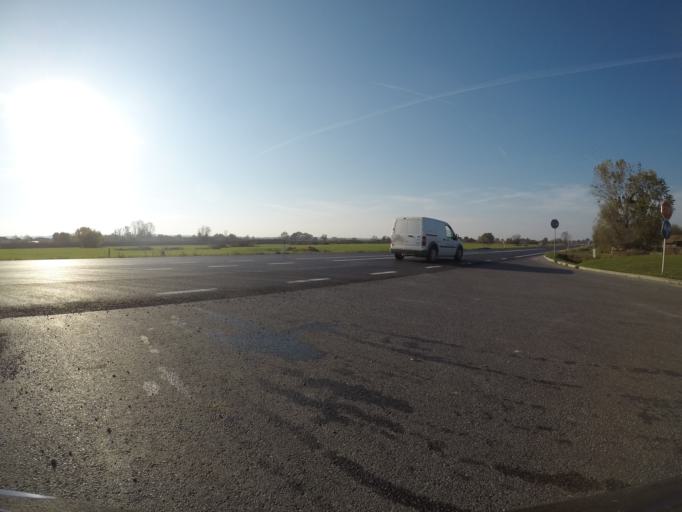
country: HR
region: Koprivnicko-Krizevacka
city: Kalinovac
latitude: 46.0337
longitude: 17.0607
